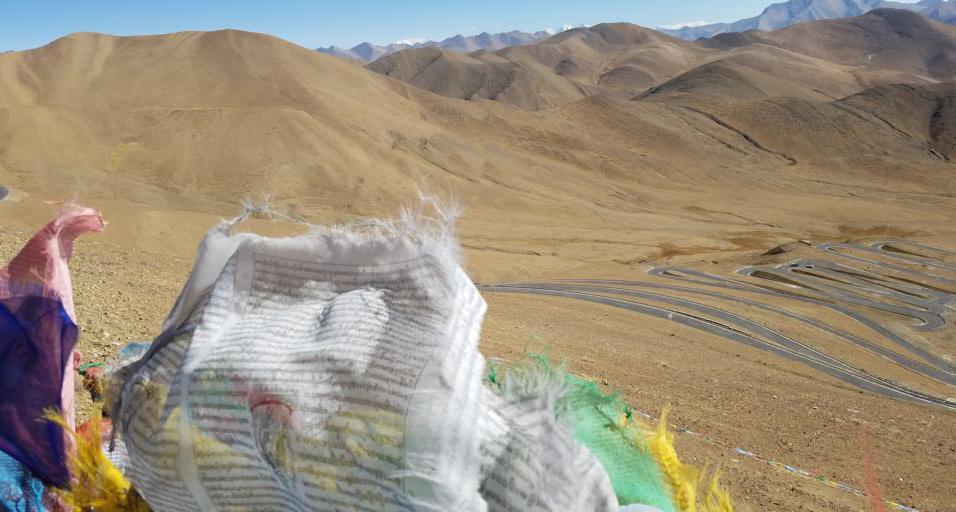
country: CN
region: Tibet Autonomous Region
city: Xegar
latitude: 28.5028
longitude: 87.0675
